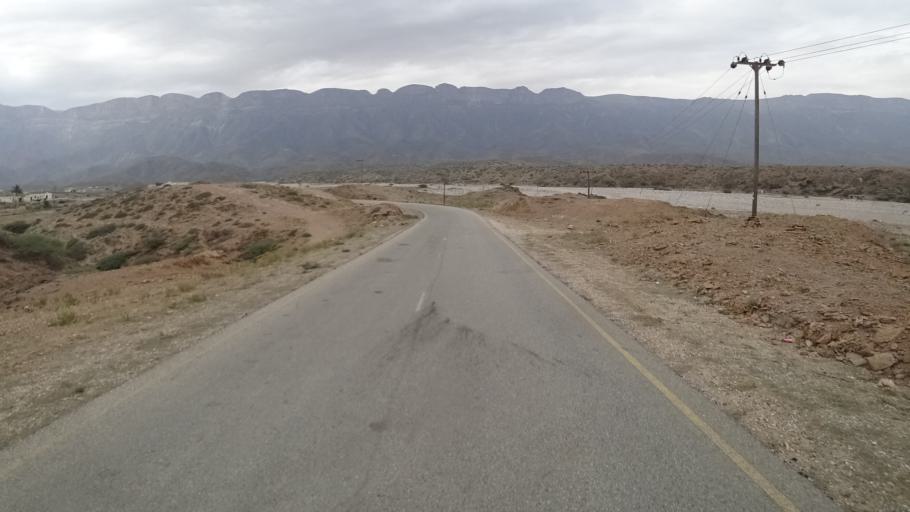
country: OM
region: Zufar
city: Salalah
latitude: 17.1570
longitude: 54.9966
